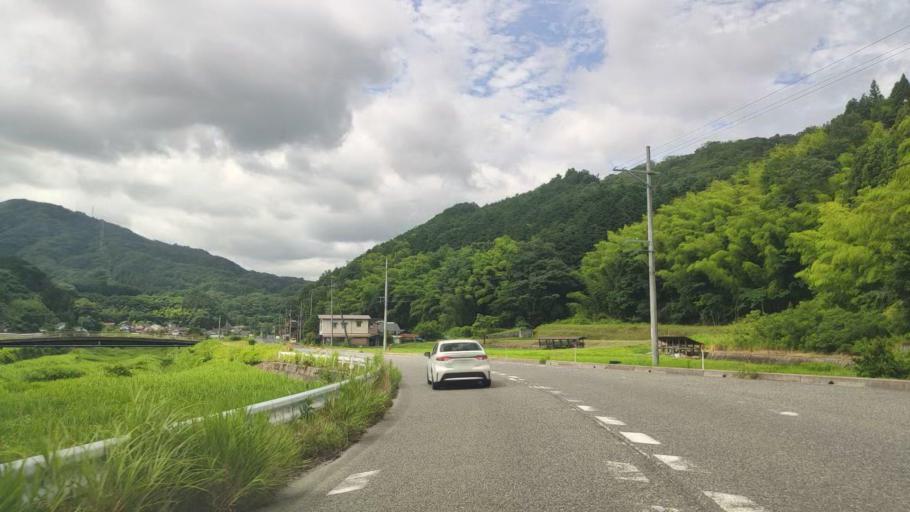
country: JP
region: Tottori
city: Yonago
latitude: 35.3257
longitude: 133.4310
